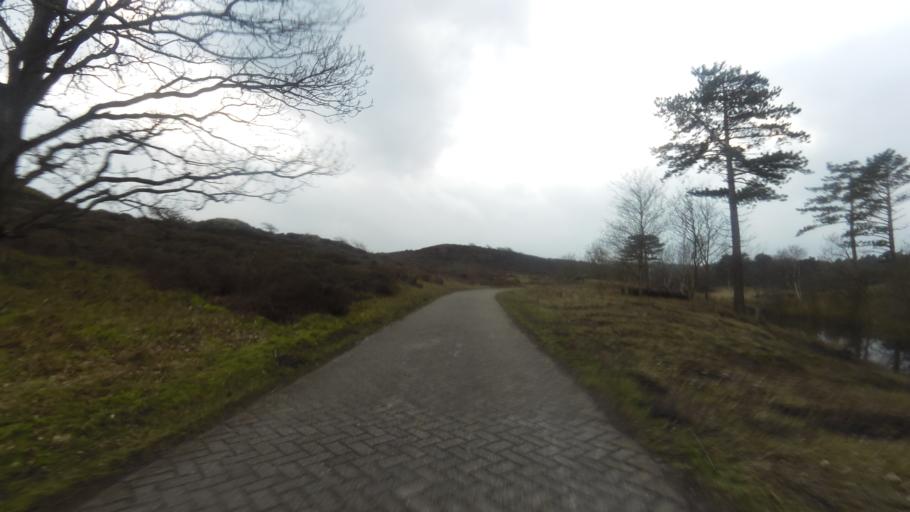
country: NL
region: North Holland
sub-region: Gemeente Bergen
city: Egmond aan Zee
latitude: 52.6721
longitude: 4.6527
